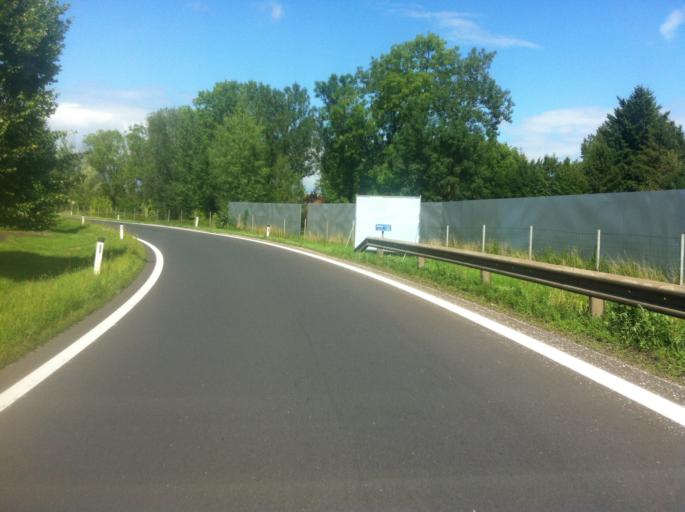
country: AT
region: Upper Austria
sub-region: Politischer Bezirk Linz-Land
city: Ansfelden
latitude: 48.2125
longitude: 14.2851
